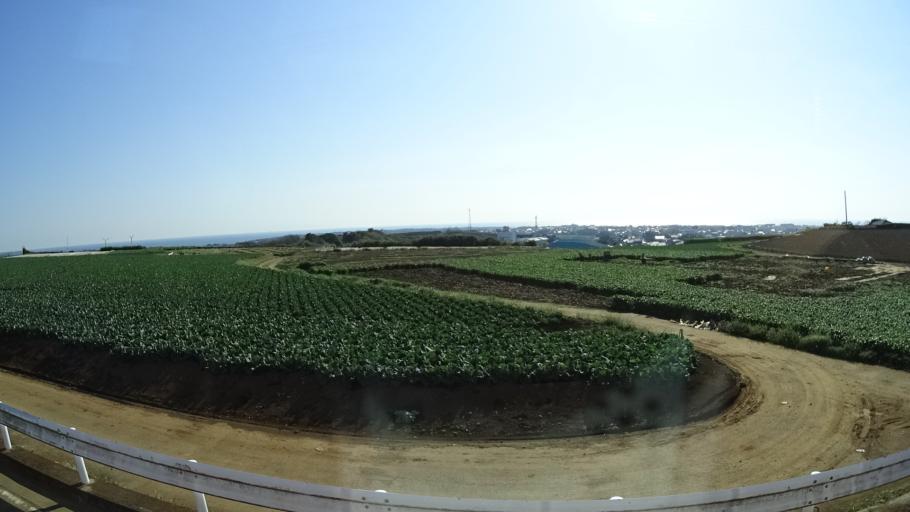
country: JP
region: Kanagawa
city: Miura
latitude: 35.1575
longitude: 139.6425
